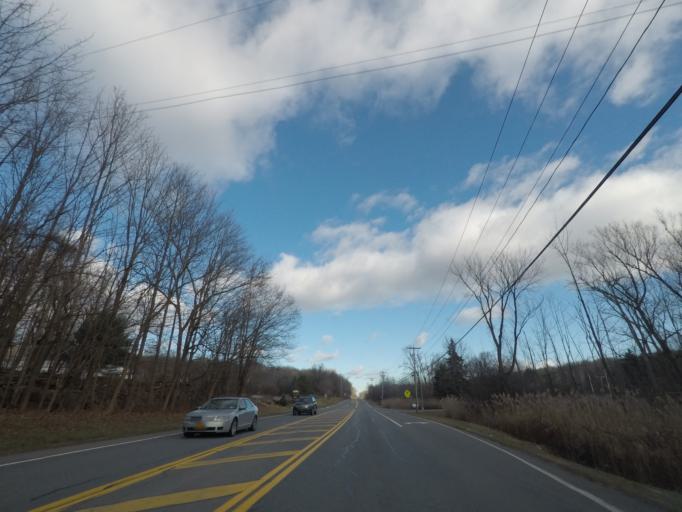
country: US
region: New York
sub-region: Saratoga County
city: Waterford
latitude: 42.7648
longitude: -73.6618
